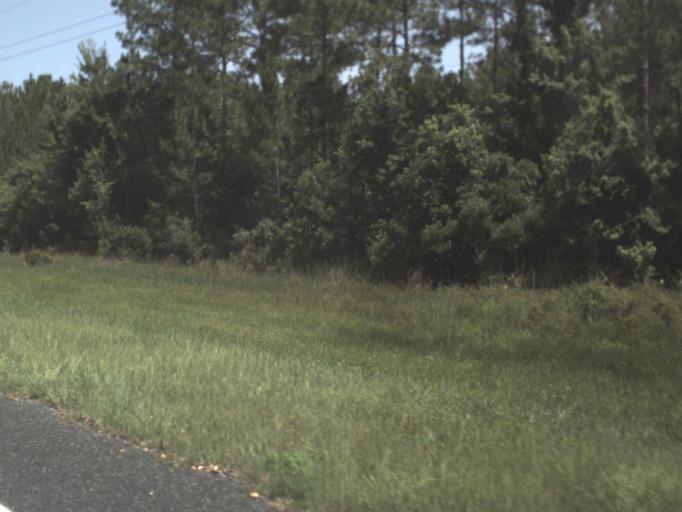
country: US
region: Florida
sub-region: Taylor County
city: Steinhatchee
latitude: 29.7057
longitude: -83.2900
